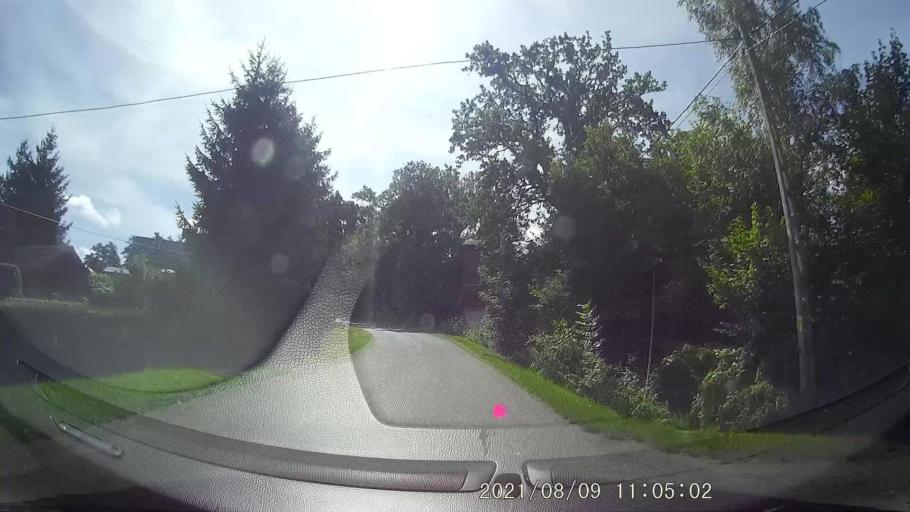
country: PL
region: Lower Silesian Voivodeship
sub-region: Powiat klodzki
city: Bozkow
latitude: 50.4611
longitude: 16.5757
